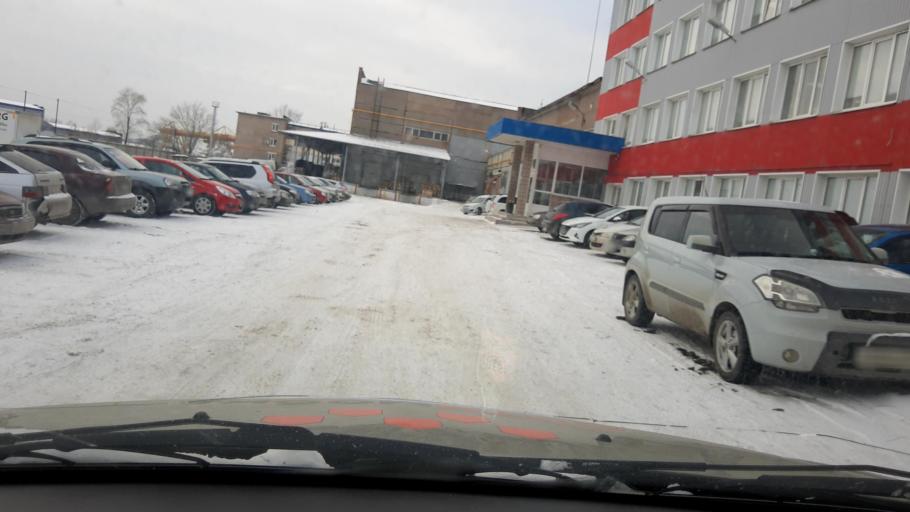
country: RU
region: Bashkortostan
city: Ufa
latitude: 54.8576
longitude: 56.0851
